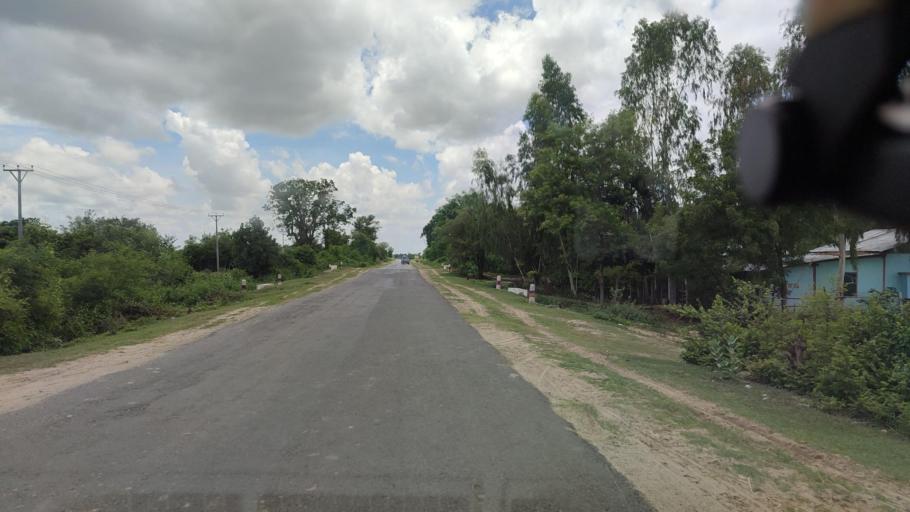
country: MM
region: Magway
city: Taungdwingyi
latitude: 20.1910
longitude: 95.4279
